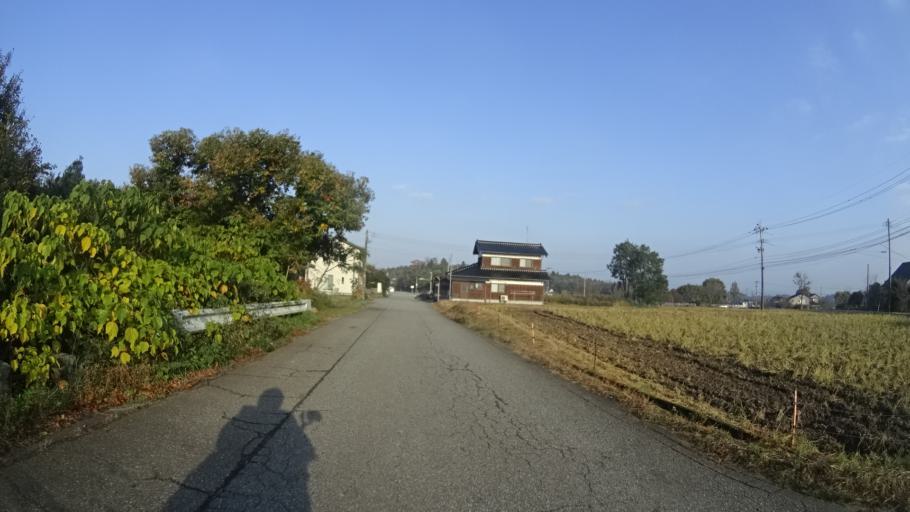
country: JP
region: Ishikawa
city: Nanao
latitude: 37.0245
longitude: 136.9775
